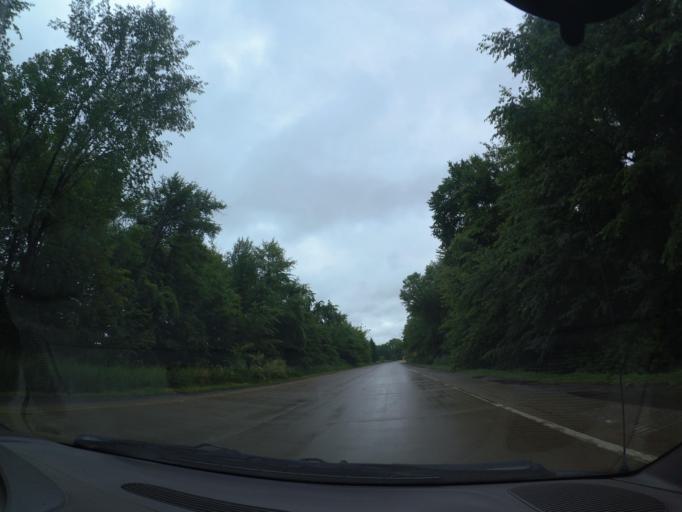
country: US
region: Ohio
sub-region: Ashtabula County
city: Conneaut
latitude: 41.9236
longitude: -80.5514
